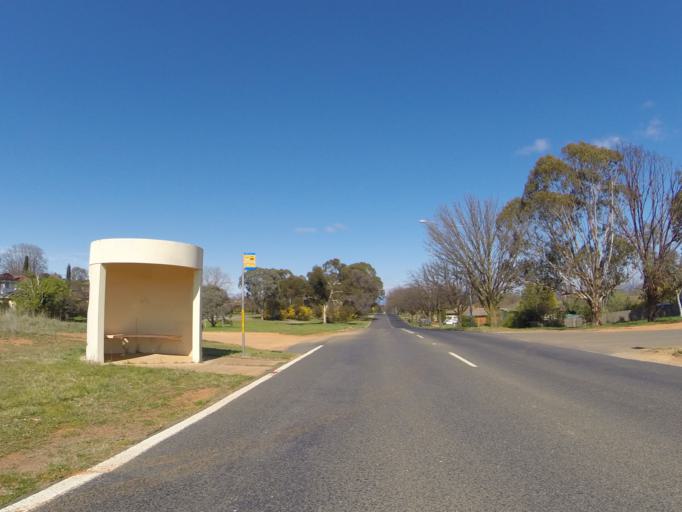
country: AU
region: Australian Capital Territory
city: Canberra
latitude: -35.2394
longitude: 149.1655
